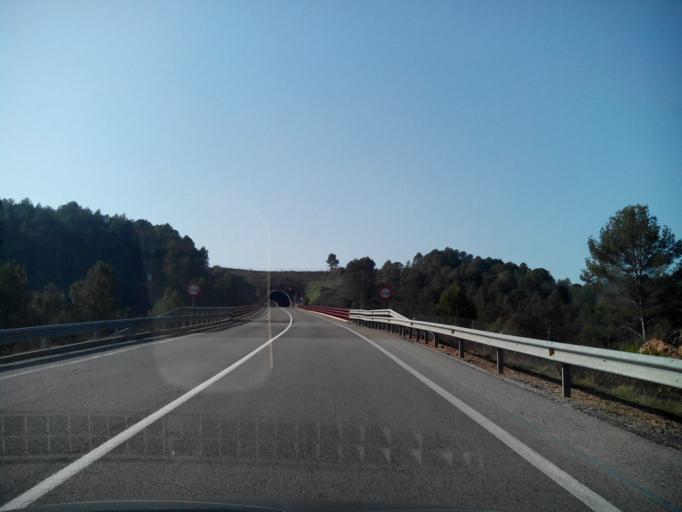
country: ES
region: Catalonia
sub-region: Provincia de Barcelona
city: Sant Salvador de Guardiola
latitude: 41.6853
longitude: 1.7556
